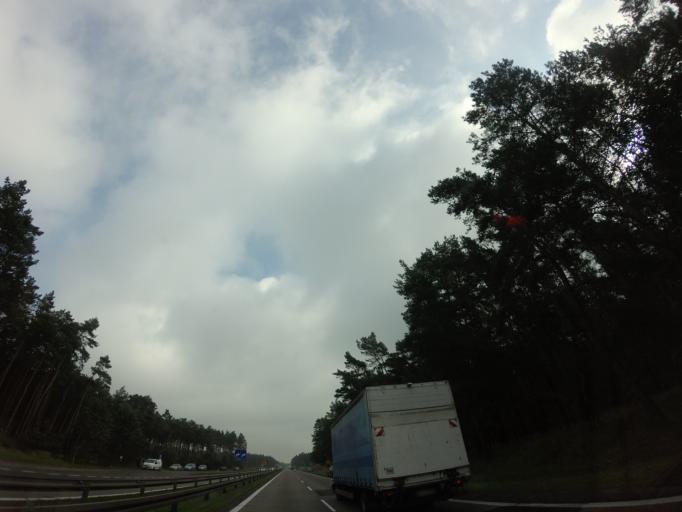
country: PL
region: West Pomeranian Voivodeship
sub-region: Powiat stargardzki
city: Kobylanka
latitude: 53.4188
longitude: 14.7554
